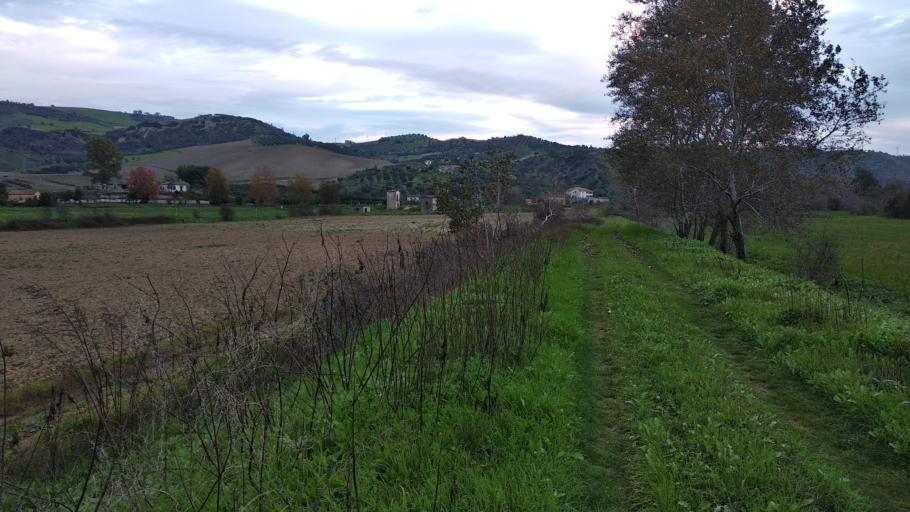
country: IT
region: Calabria
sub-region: Provincia di Cosenza
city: Tarsia
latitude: 39.6027
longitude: 16.2609
